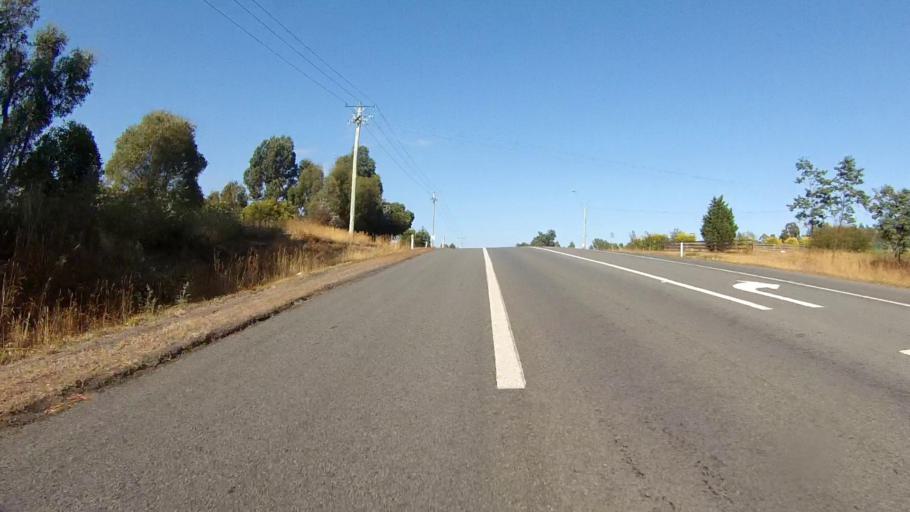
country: AU
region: Tasmania
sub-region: Derwent Valley
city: New Norfolk
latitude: -42.7635
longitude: 147.1323
